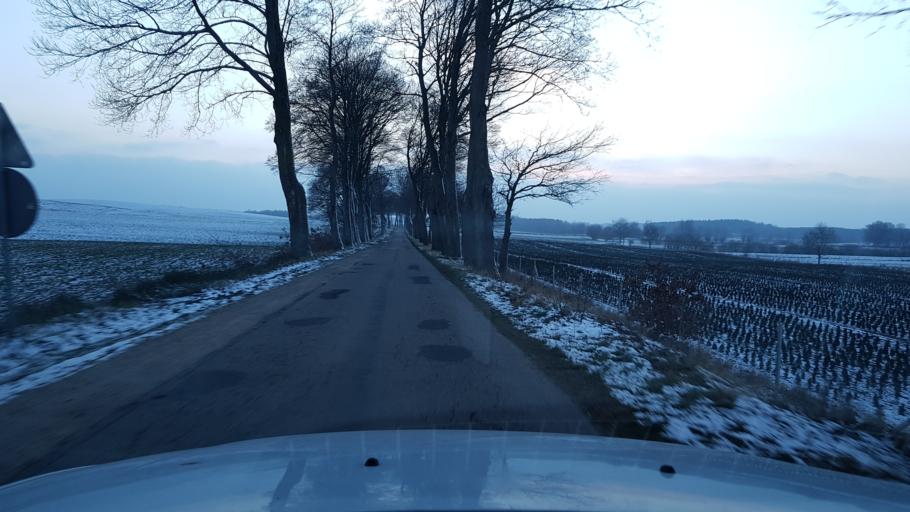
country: PL
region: West Pomeranian Voivodeship
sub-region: Powiat swidwinski
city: Slawoborze
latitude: 53.9681
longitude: 15.7614
